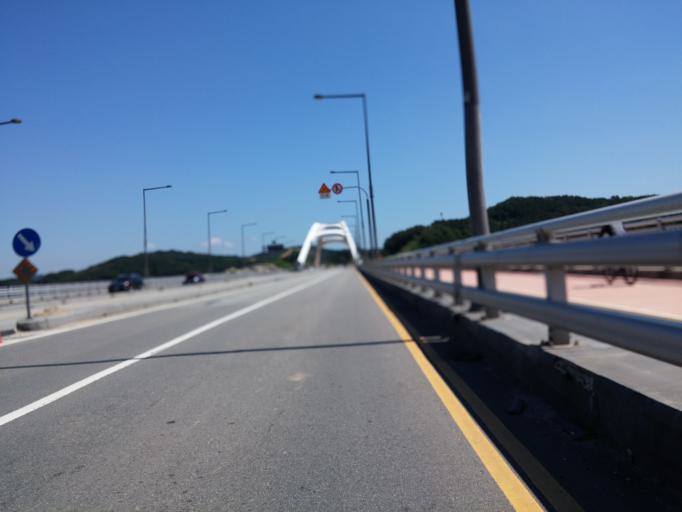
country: KR
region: Daejeon
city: Songgang-dong
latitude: 36.5347
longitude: 127.2964
